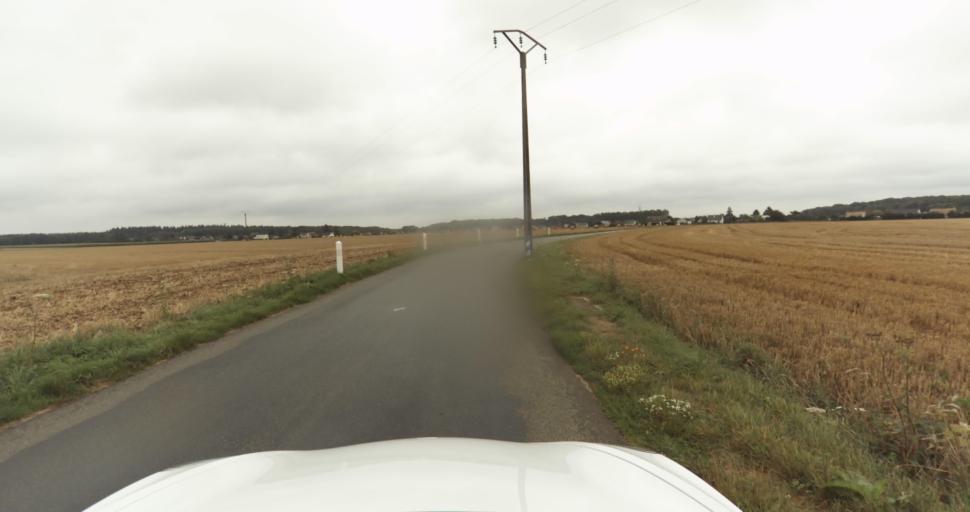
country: FR
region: Haute-Normandie
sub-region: Departement de l'Eure
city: Aviron
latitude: 49.0650
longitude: 1.1212
